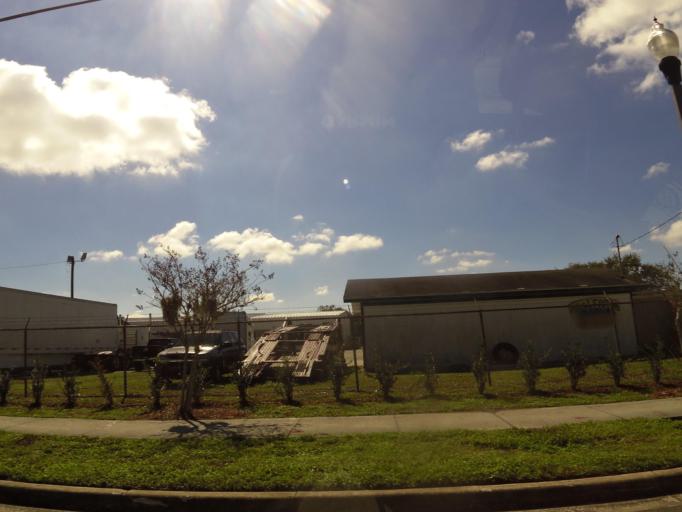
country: US
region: Florida
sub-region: Seminole County
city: Sanford
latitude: 28.8008
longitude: -81.2755
